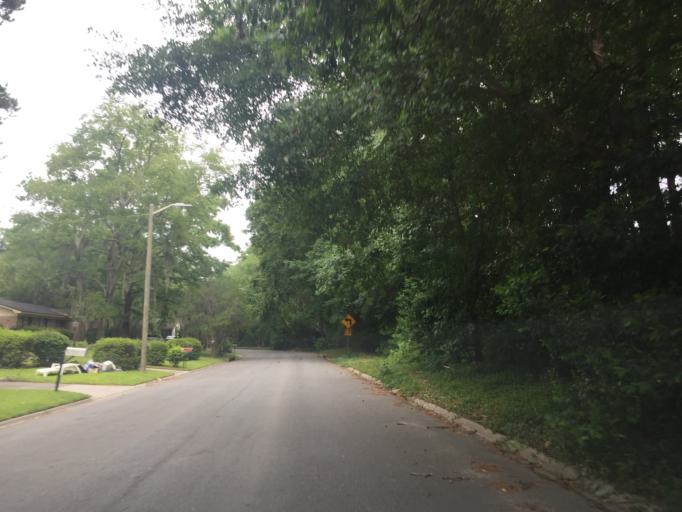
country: US
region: Georgia
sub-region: Chatham County
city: Montgomery
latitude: 31.9845
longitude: -81.1284
